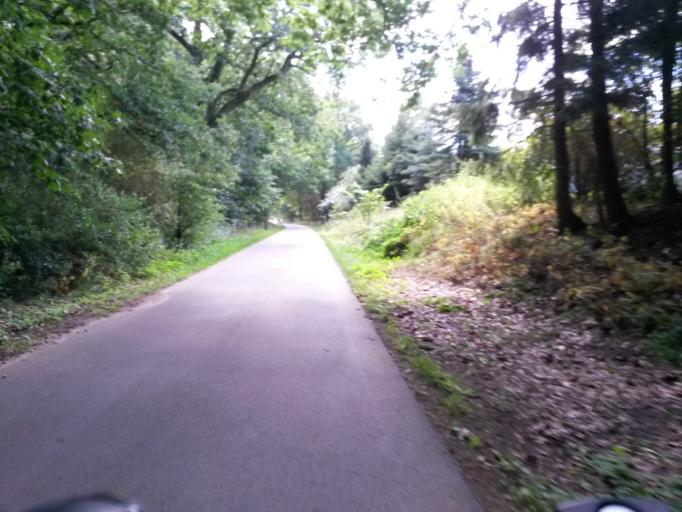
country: DE
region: Brandenburg
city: Templin
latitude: 53.1768
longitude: 13.5146
